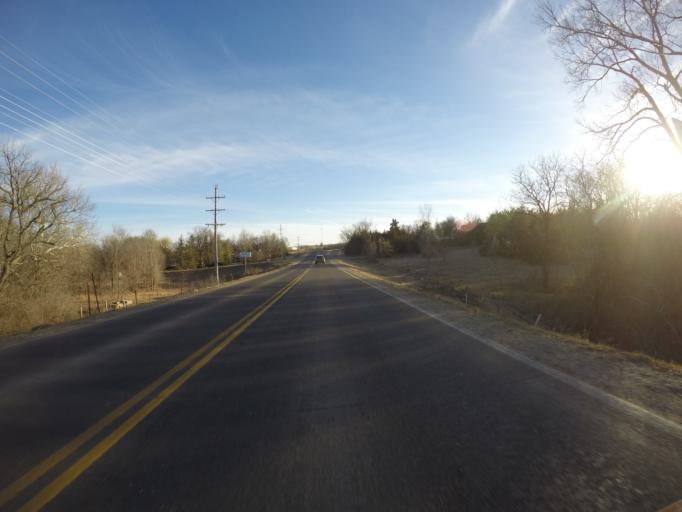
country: US
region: Kansas
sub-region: Marshall County
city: Marysville
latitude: 39.8455
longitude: -96.6668
